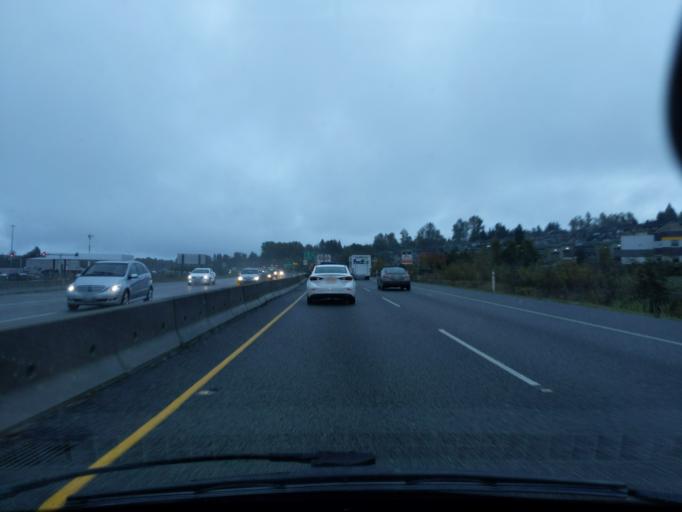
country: CA
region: British Columbia
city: Pitt Meadows
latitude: 49.1940
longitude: -122.7430
